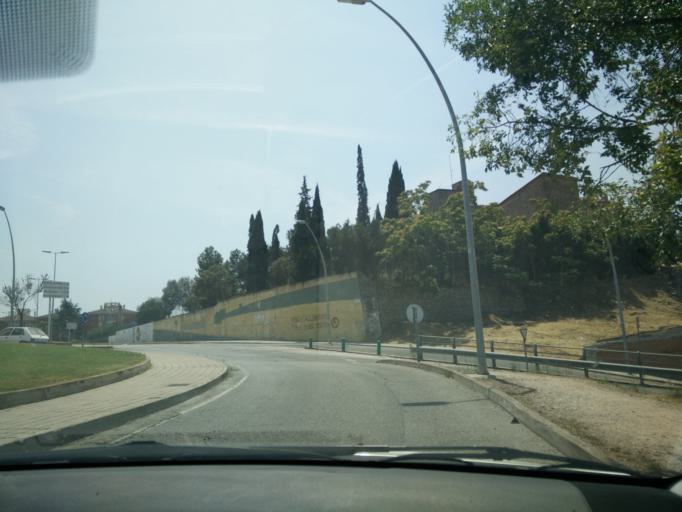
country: ES
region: Catalonia
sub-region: Provincia de Barcelona
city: Manresa
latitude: 41.7212
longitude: 1.8405
